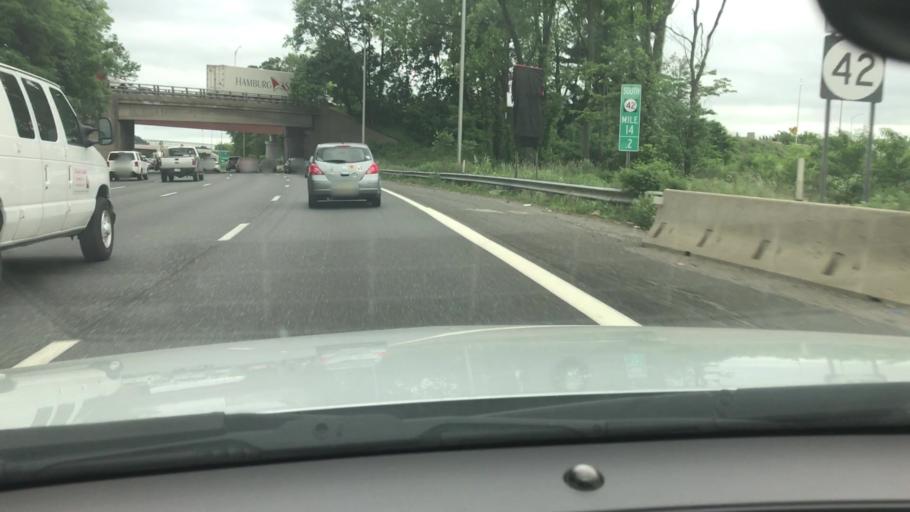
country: US
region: New Jersey
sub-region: Camden County
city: Bellmawr
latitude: 39.8682
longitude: -75.1022
